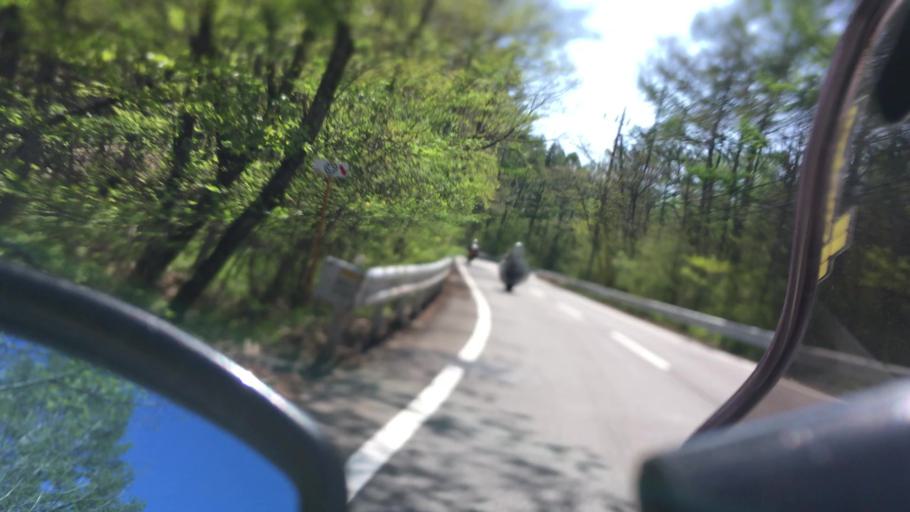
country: JP
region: Nagano
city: Komoro
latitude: 36.4647
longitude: 138.5443
